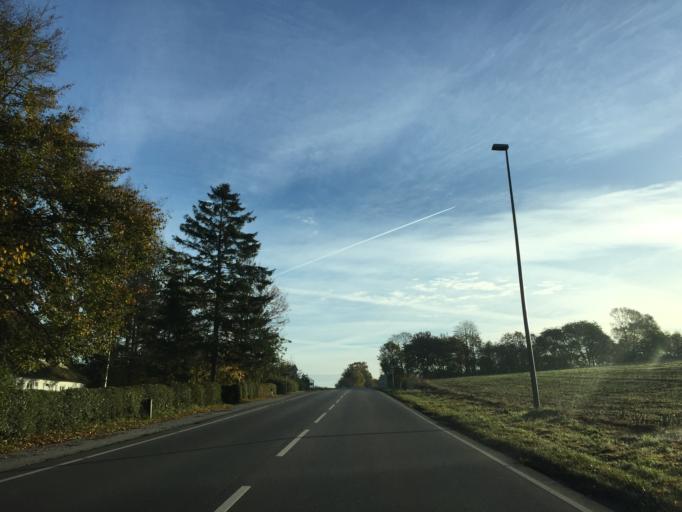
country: DK
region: Central Jutland
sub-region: Skanderborg Kommune
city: Galten
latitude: 56.1101
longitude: 9.8847
